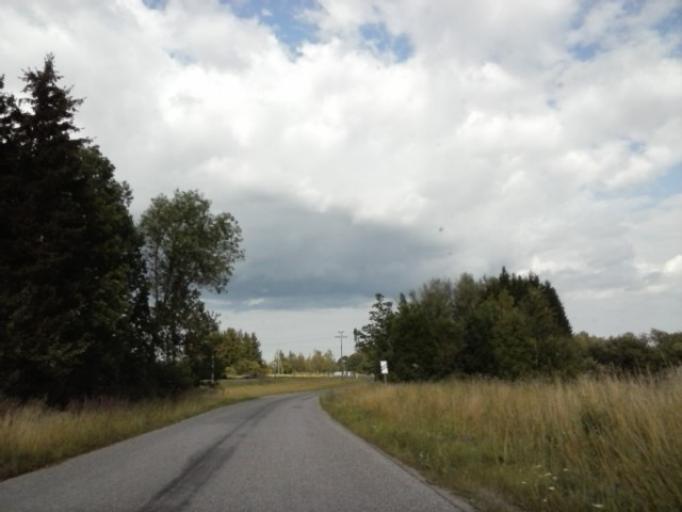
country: EE
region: Vorumaa
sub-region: Voru linn
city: Voru
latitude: 57.8395
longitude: 27.1572
